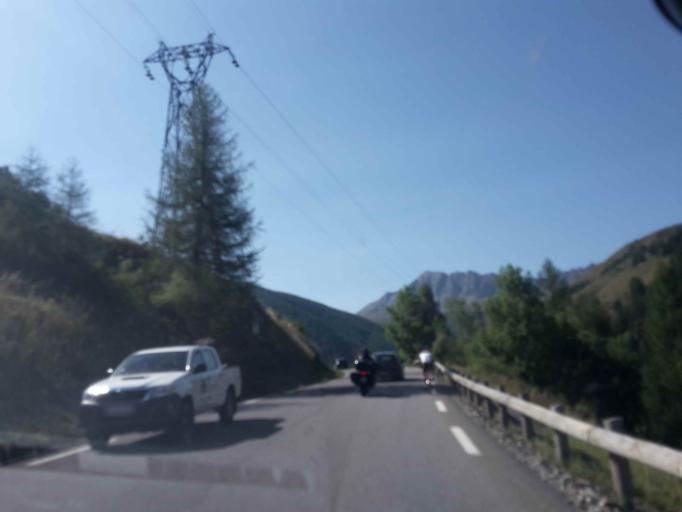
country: FR
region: Provence-Alpes-Cote d'Azur
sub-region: Departement des Hautes-Alpes
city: Guillestre
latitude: 44.6026
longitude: 6.6890
